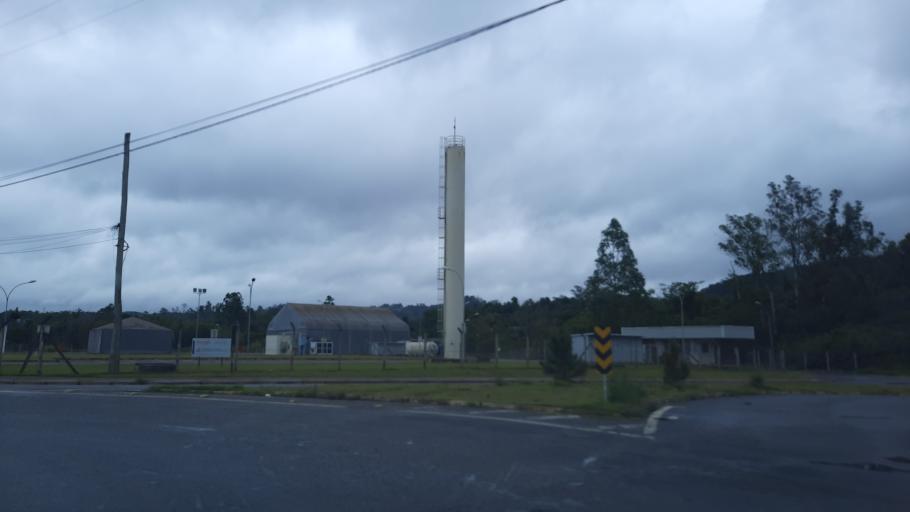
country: BR
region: Sao Paulo
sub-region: Atibaia
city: Atibaia
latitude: -23.1838
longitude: -46.5824
